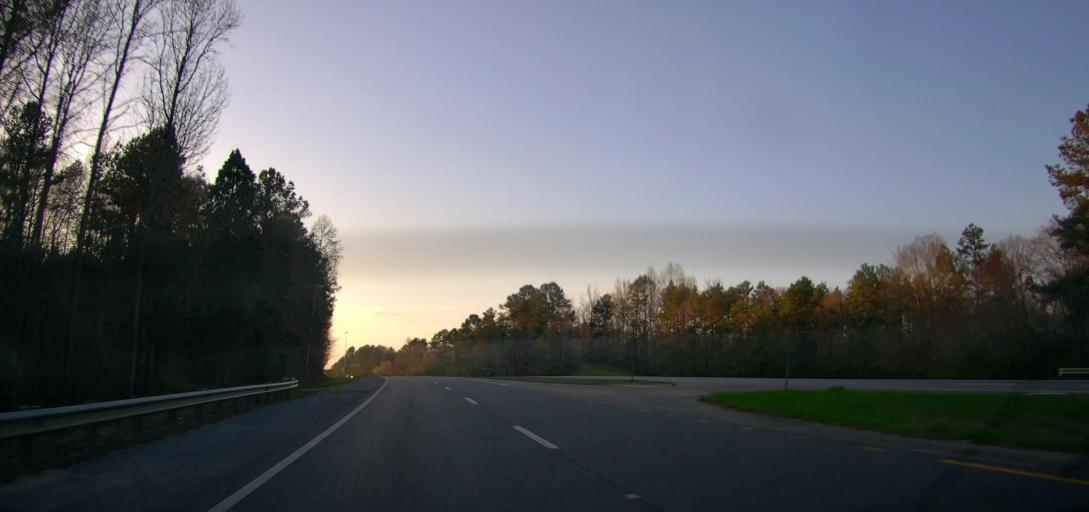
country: US
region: Alabama
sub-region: Talladega County
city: Sylacauga
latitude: 33.1391
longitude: -86.2502
